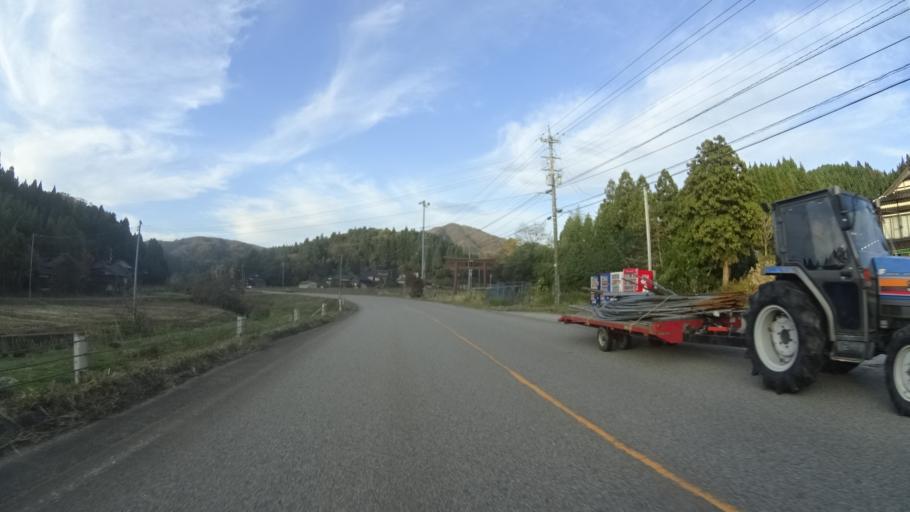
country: JP
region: Ishikawa
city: Nanao
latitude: 37.1911
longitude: 136.7169
